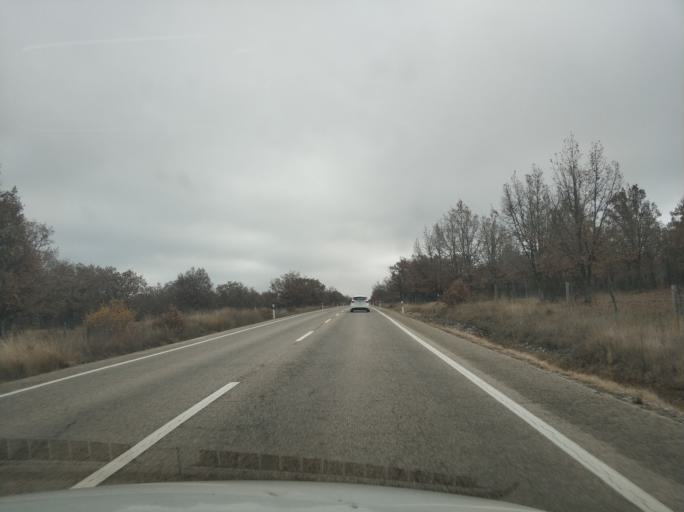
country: ES
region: Castille and Leon
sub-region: Provincia de Soria
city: Golmayo
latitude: 41.8026
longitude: -2.5644
